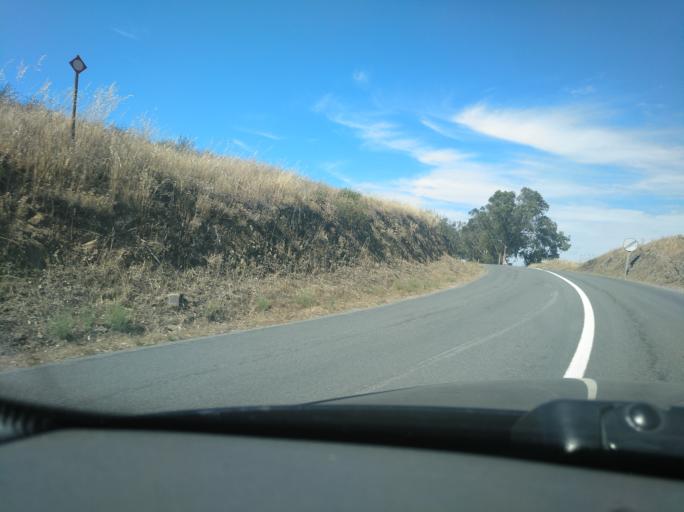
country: PT
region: Beja
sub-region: Mertola
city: Mertola
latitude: 37.6162
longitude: -7.7782
